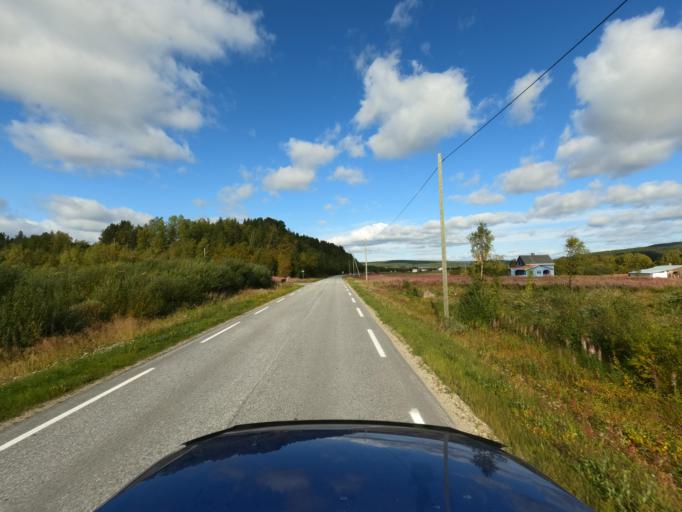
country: NO
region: Finnmark Fylke
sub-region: Karasjok
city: Karasjohka
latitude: 69.4065
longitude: 25.8085
